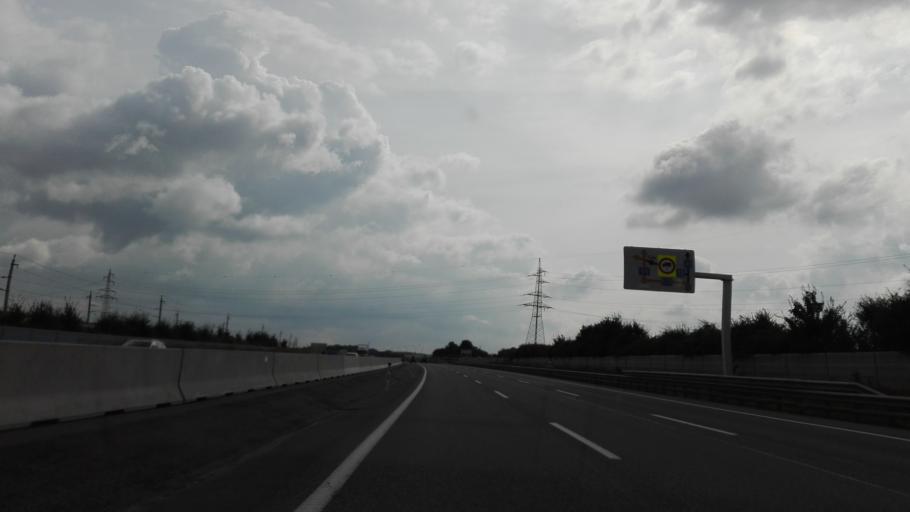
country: AT
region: Lower Austria
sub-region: Sankt Polten Stadt
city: Sankt Poelten
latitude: 48.1760
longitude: 15.6458
